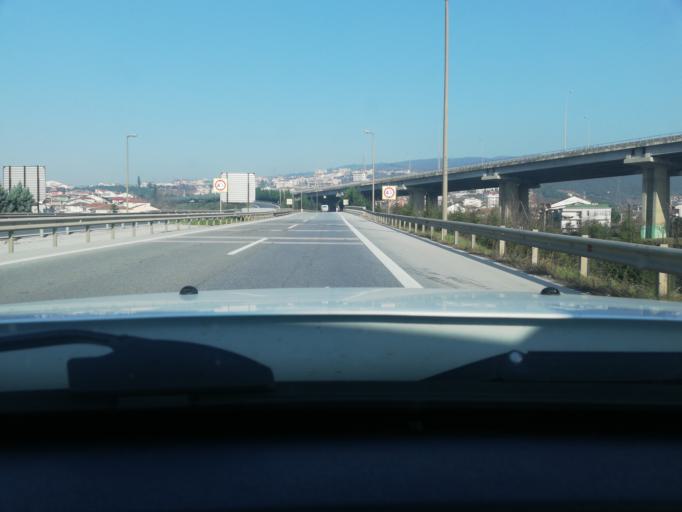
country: TR
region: Kocaeli
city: Derince
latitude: 40.7651
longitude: 29.8550
